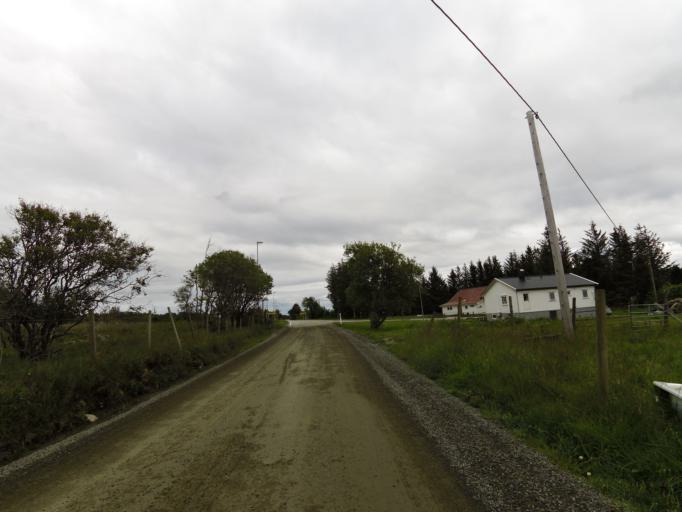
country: NO
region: Vest-Agder
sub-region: Farsund
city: Vestbygd
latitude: 58.1280
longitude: 6.6136
